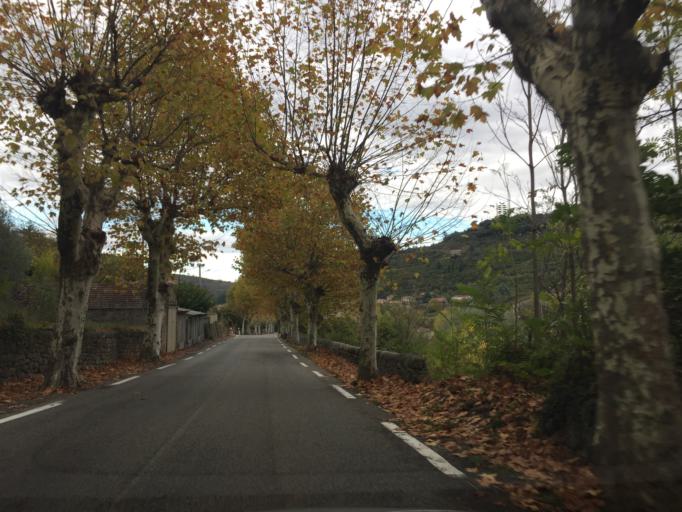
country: FR
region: Rhone-Alpes
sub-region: Departement de l'Ardeche
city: Les Vans
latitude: 44.4059
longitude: 4.1212
